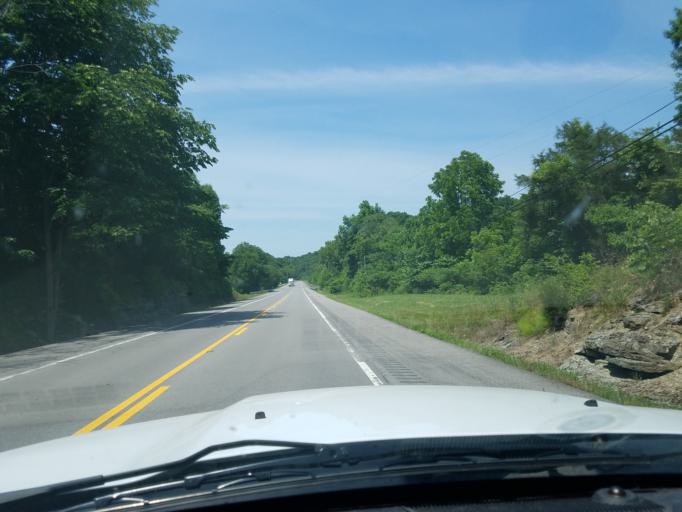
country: US
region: Tennessee
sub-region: Sumner County
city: Westmoreland
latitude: 36.6197
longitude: -86.2368
